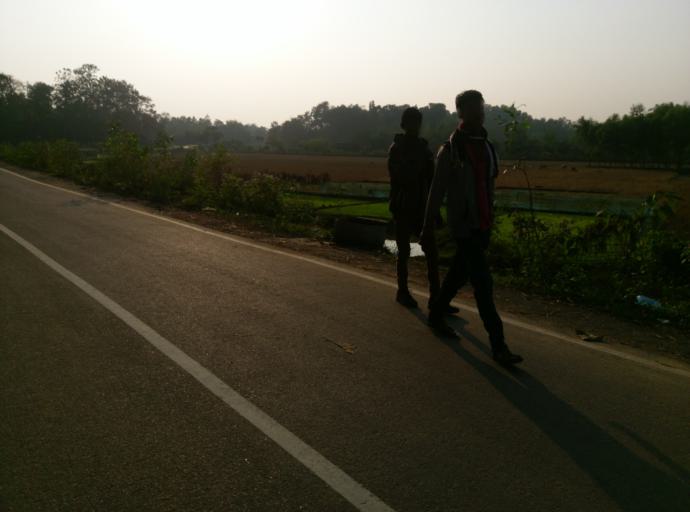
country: BD
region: Dhaka
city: Netrakona
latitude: 25.1749
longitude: 90.6482
